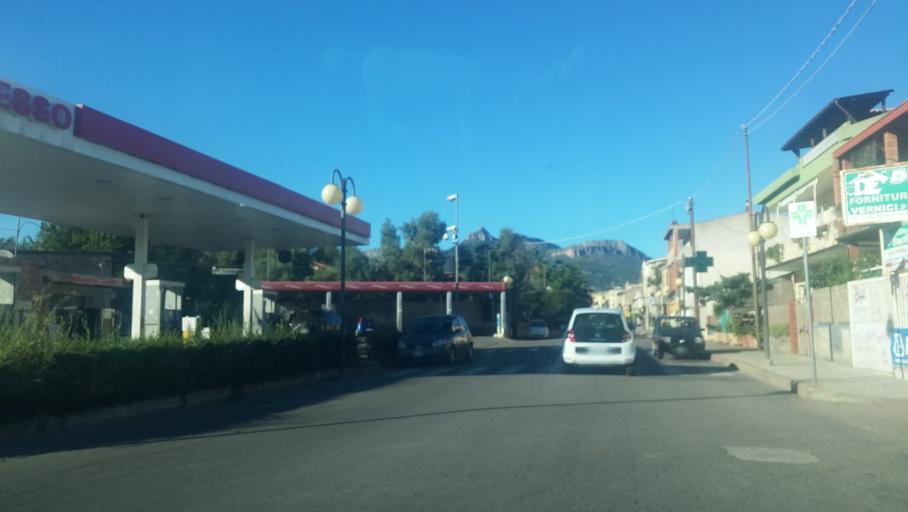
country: IT
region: Sardinia
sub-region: Provincia di Ogliastra
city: Lotzorai
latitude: 39.9679
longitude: 9.6601
